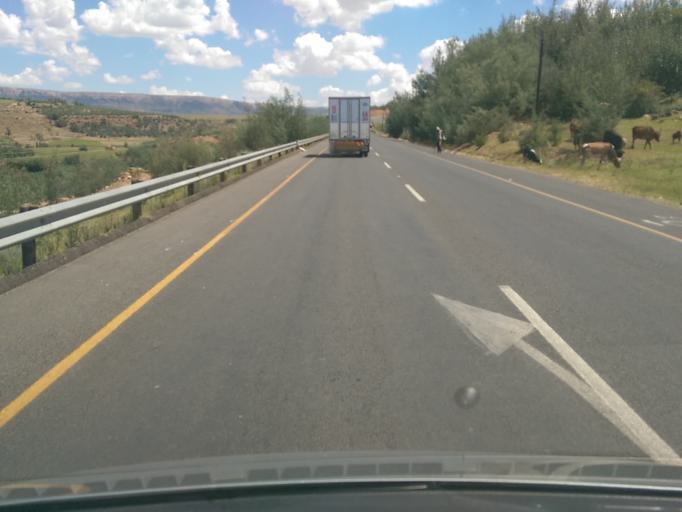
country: LS
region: Maseru
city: Maseru
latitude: -29.3988
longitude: 27.5339
